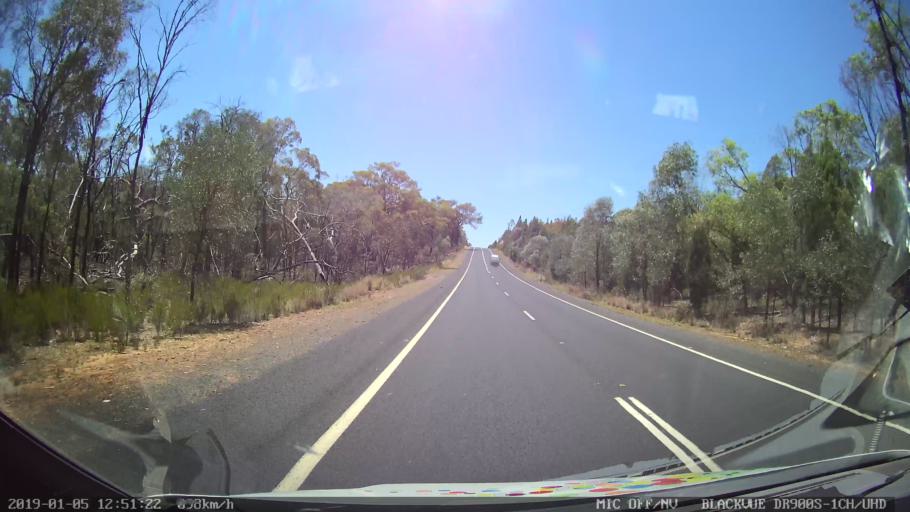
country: AU
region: New South Wales
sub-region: Warrumbungle Shire
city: Coonabarabran
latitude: -31.1208
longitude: 149.6383
